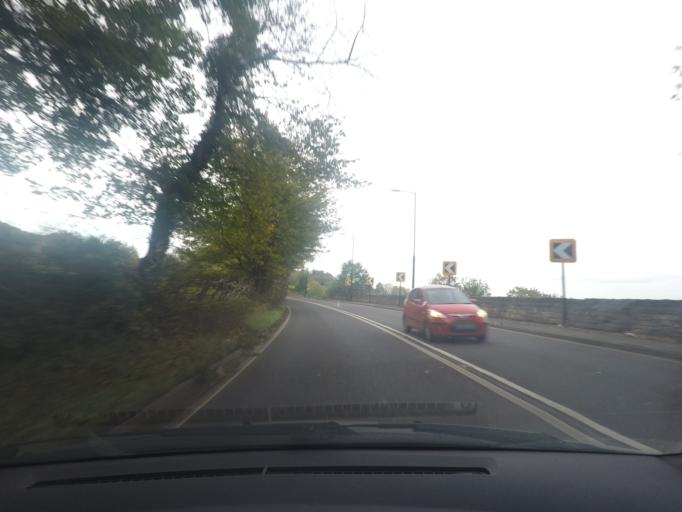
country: GB
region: England
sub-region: Sheffield
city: Chapletown
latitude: 53.4507
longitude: -1.4932
